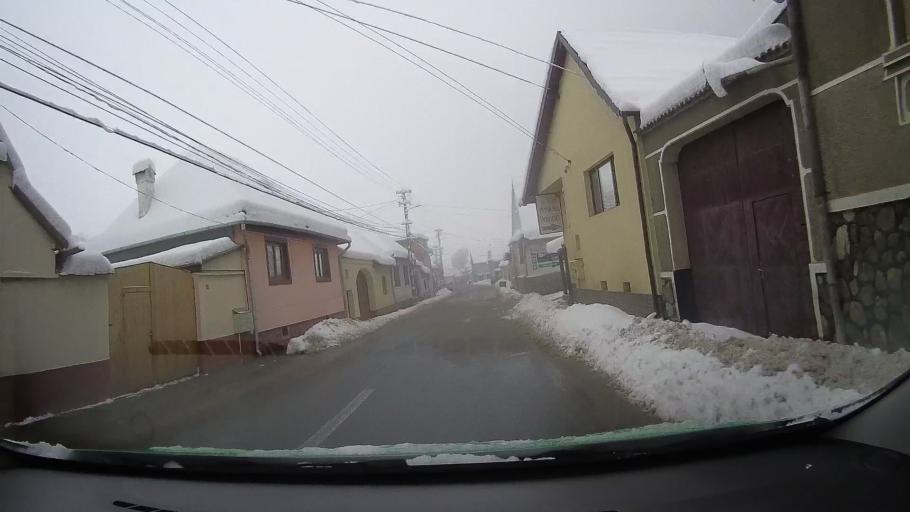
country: RO
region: Sibiu
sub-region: Oras Saliste
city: Saliste
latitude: 45.7956
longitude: 23.8720
